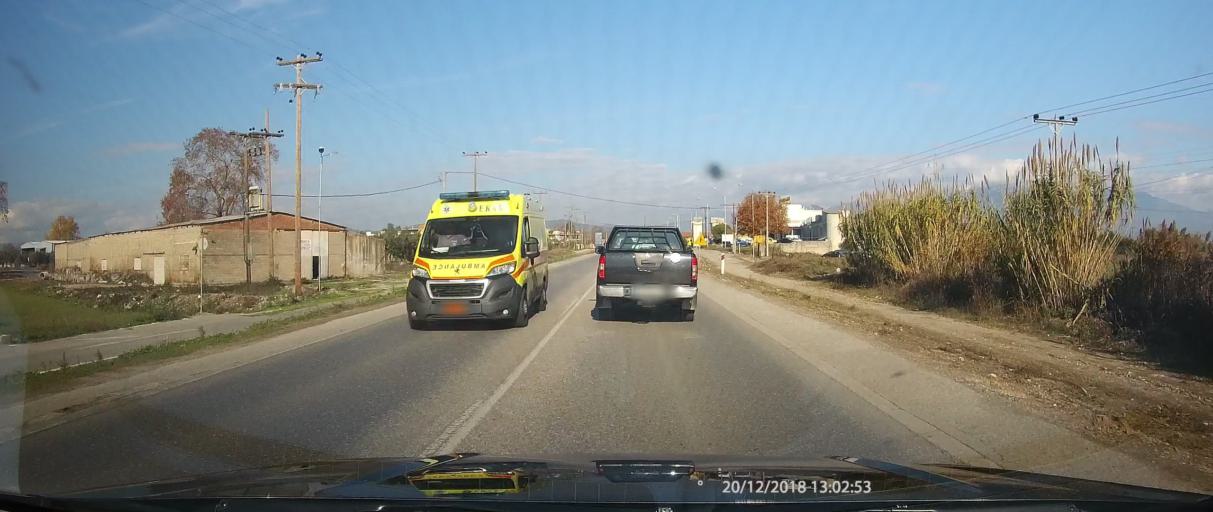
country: GR
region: West Greece
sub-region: Nomos Aitolias kai Akarnanias
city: Panaitolion
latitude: 38.5757
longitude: 21.4246
